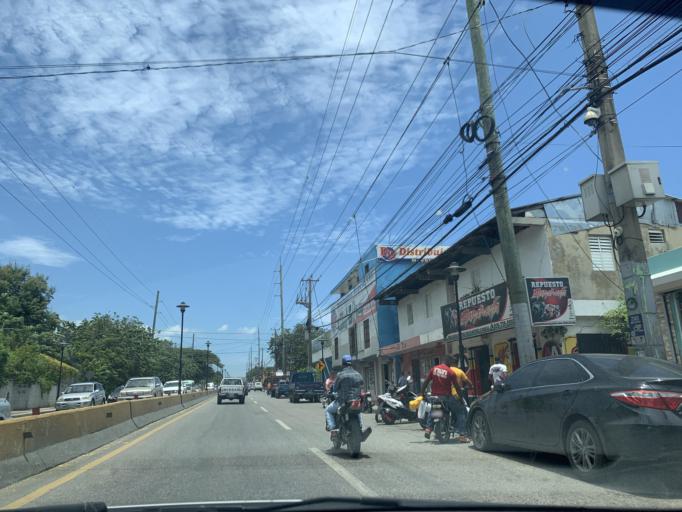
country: DO
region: Puerto Plata
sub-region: Puerto Plata
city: Puerto Plata
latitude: 19.7931
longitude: -70.7090
